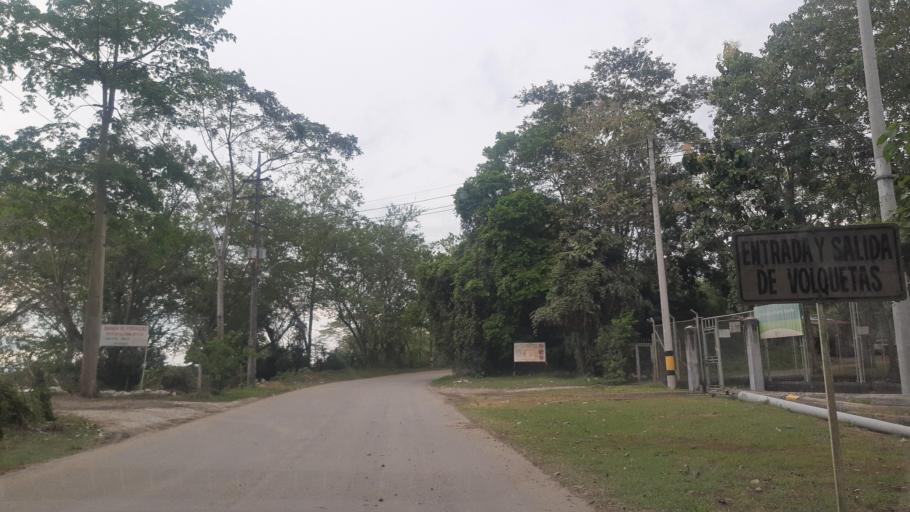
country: CO
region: Antioquia
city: Puerto Triunfo
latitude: 5.8774
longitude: -74.6357
